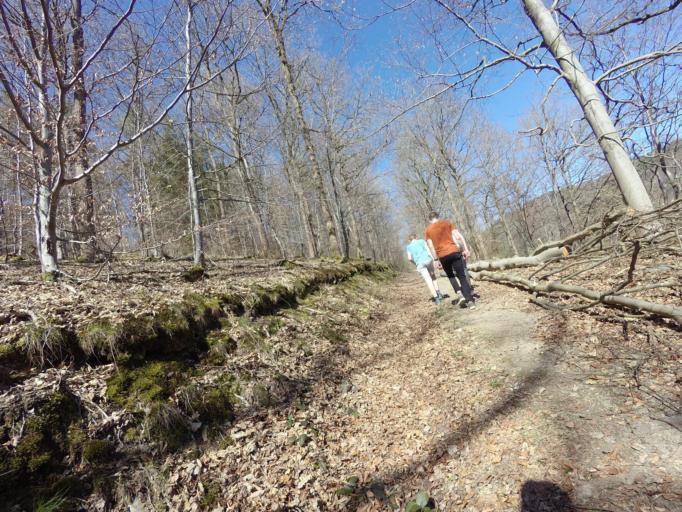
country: BE
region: Wallonia
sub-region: Province de Liege
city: Trois-Ponts
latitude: 50.3871
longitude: 5.8687
